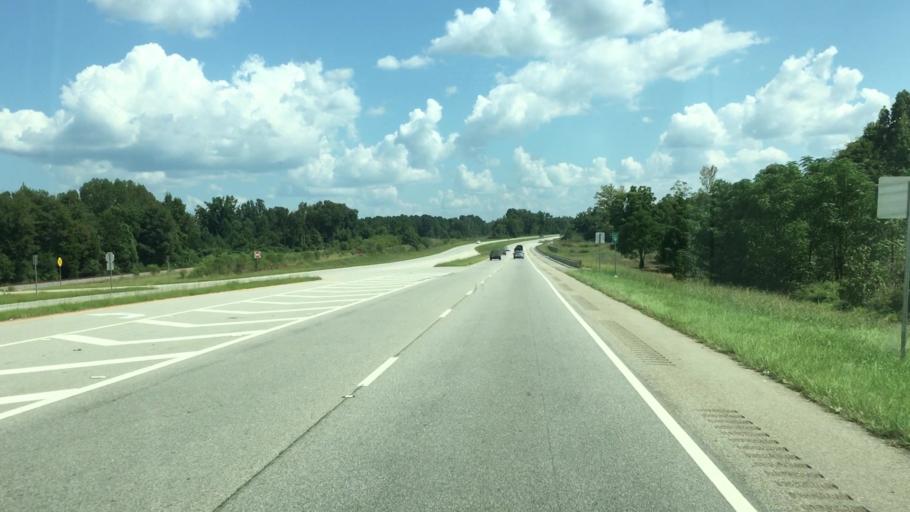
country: US
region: Georgia
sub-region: Putnam County
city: Eatonton
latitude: 33.2921
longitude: -83.3760
